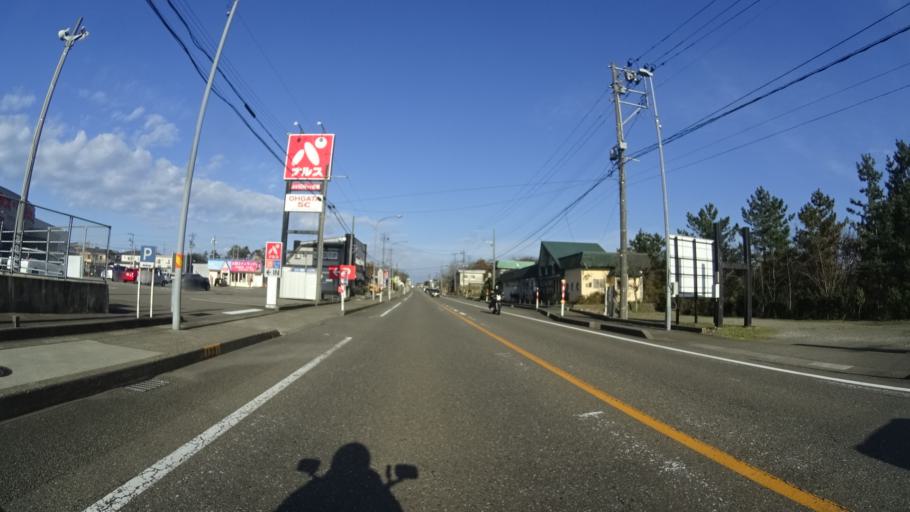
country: JP
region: Niigata
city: Joetsu
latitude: 37.2279
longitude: 138.3314
